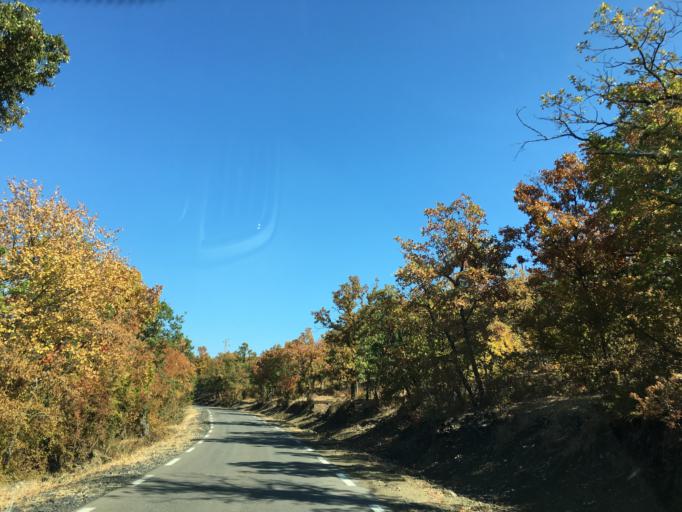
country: BG
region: Kurdzhali
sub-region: Obshtina Krumovgrad
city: Krumovgrad
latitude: 41.4852
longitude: 25.5277
